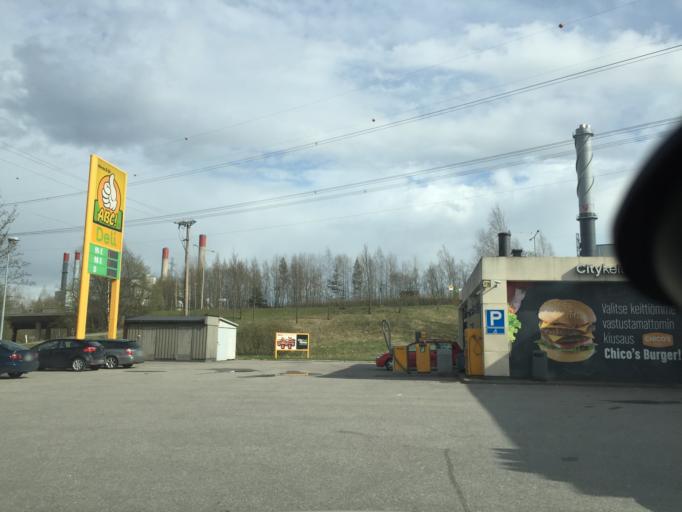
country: FI
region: Uusimaa
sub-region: Helsinki
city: Kilo
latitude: 60.2846
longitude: 24.8265
